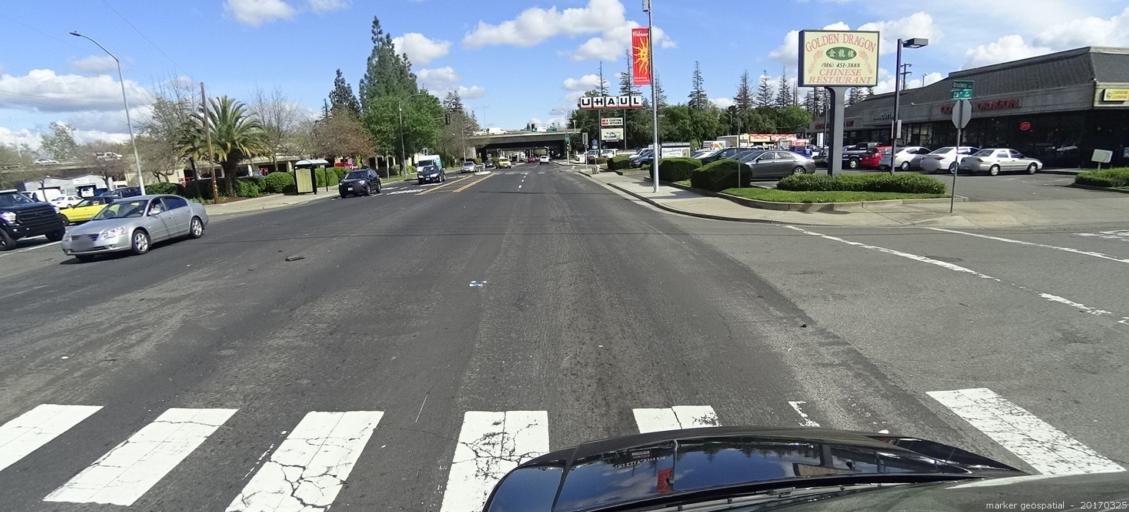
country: US
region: California
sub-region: Sacramento County
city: Sacramento
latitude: 38.5574
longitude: -121.4767
